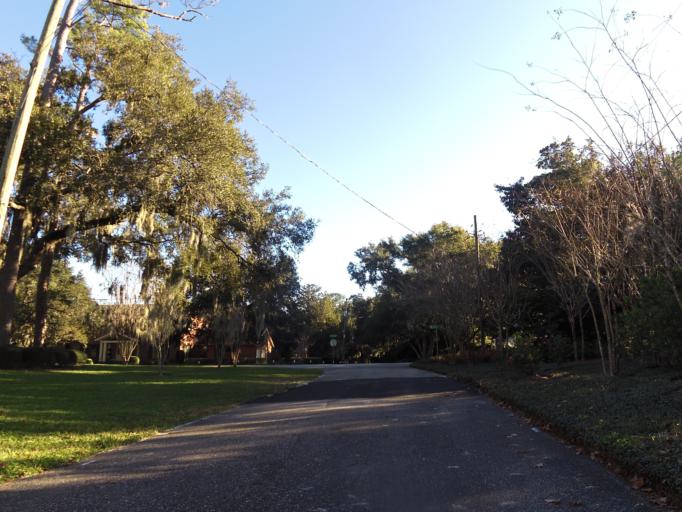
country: US
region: Florida
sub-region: Duval County
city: Jacksonville
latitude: 30.2813
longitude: -81.7005
